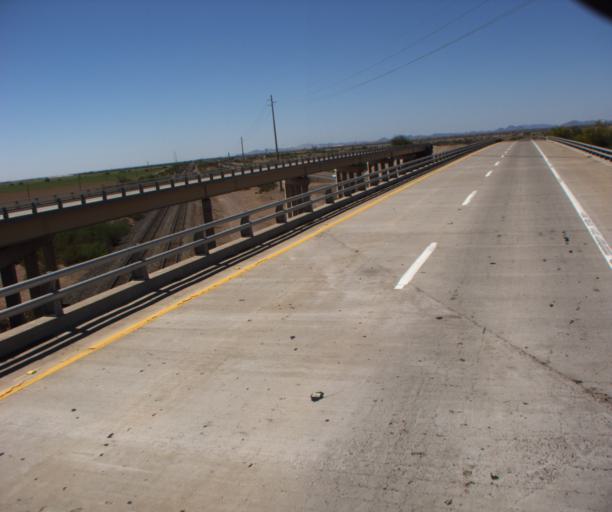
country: US
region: Arizona
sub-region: Maricopa County
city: Gila Bend
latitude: 32.9420
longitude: -112.7400
